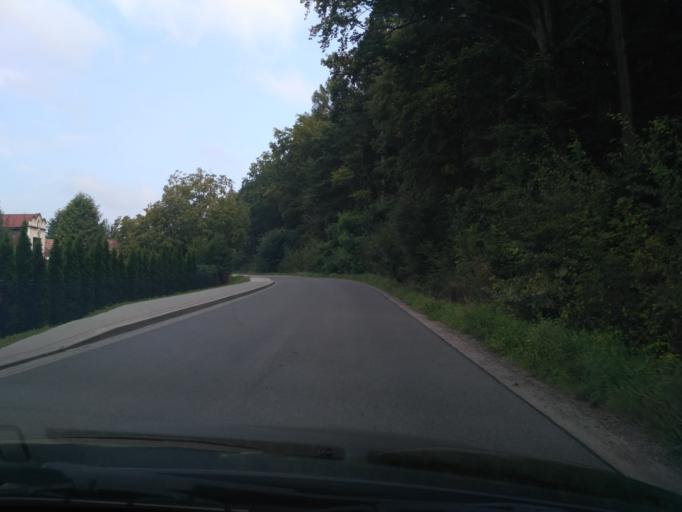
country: PL
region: Subcarpathian Voivodeship
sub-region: Powiat strzyzowski
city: Czudec
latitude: 49.9593
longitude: 21.8453
